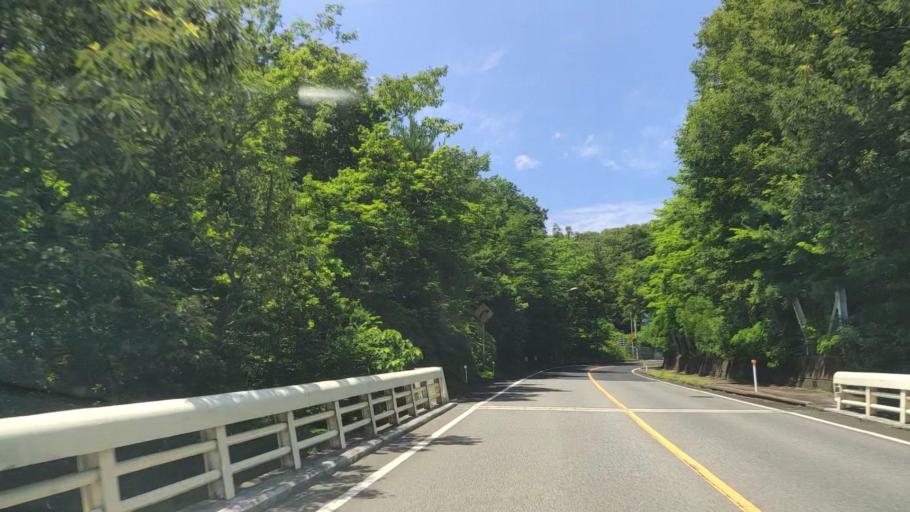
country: JP
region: Tottori
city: Tottori
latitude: 35.5293
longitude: 134.2293
